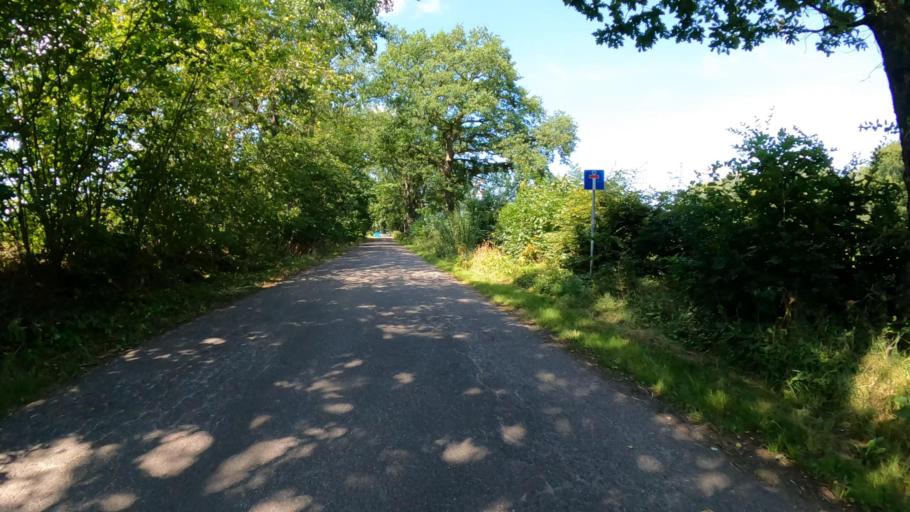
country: DE
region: Schleswig-Holstein
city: Halstenbek
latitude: 53.6228
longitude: 9.8596
